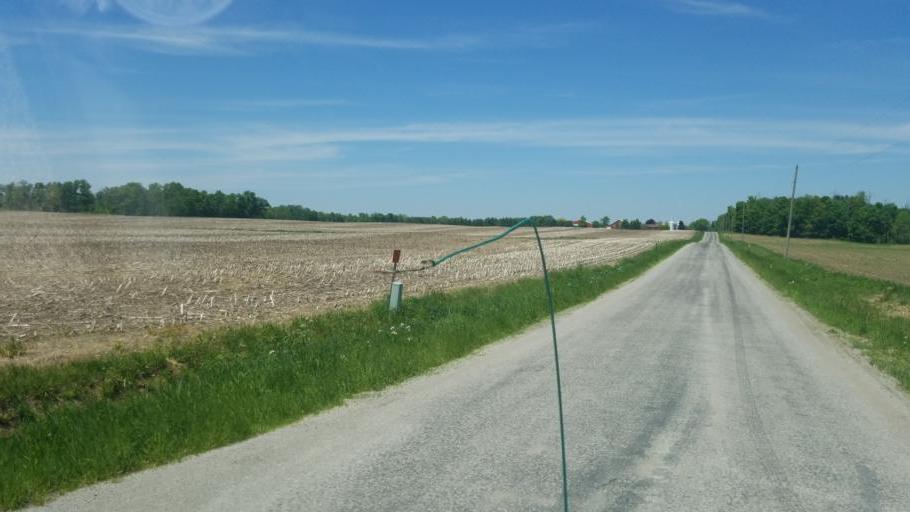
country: US
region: Ohio
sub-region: Huron County
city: New London
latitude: 41.0111
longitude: -82.4338
